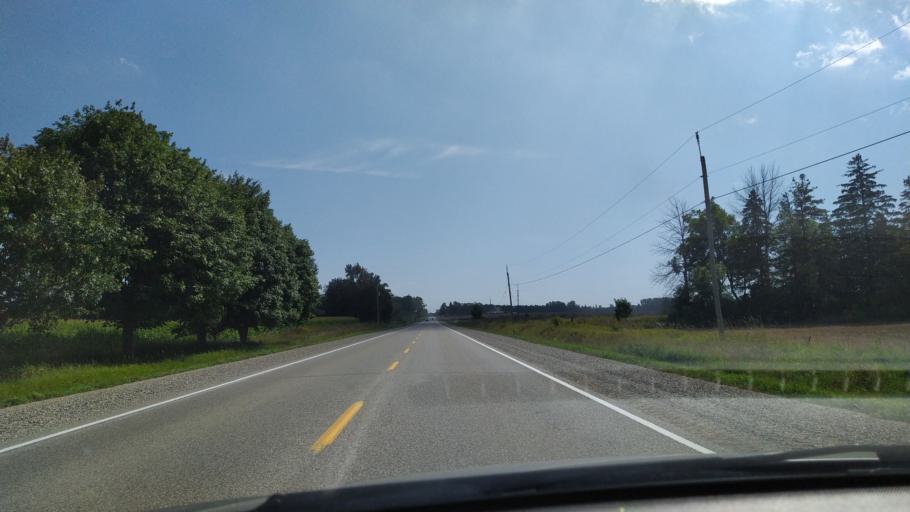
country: CA
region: Ontario
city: Ingersoll
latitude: 43.1134
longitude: -80.8803
